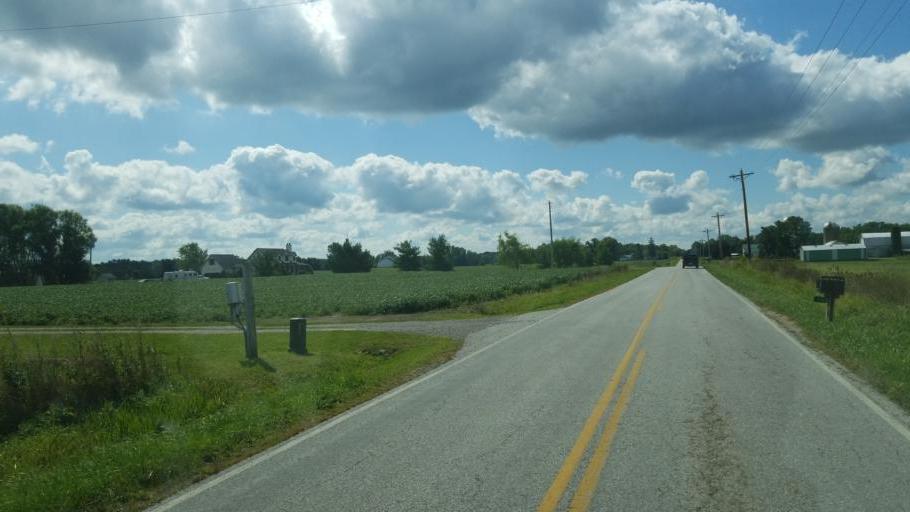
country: US
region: Ohio
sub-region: Lorain County
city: Lagrange
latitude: 41.1283
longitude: -82.0938
